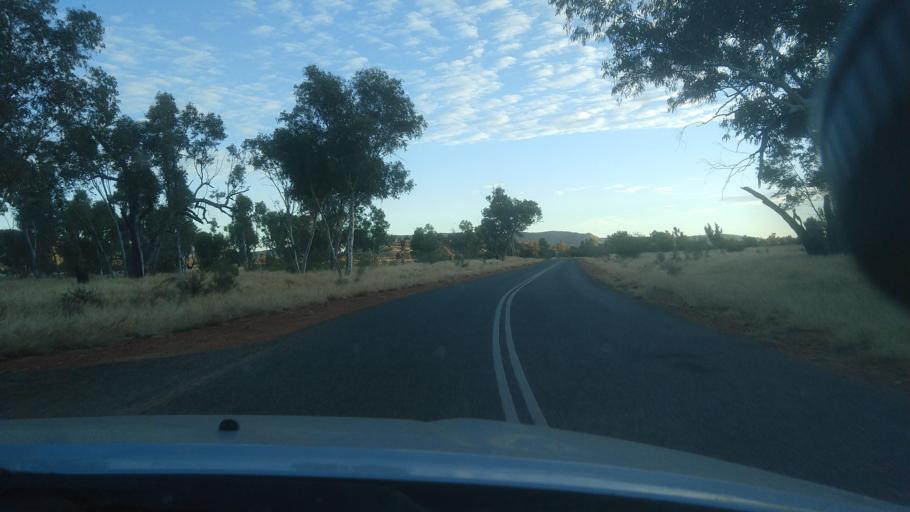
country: AU
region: Northern Territory
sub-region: Alice Springs
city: Alice Springs
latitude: -23.7386
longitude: 133.7419
